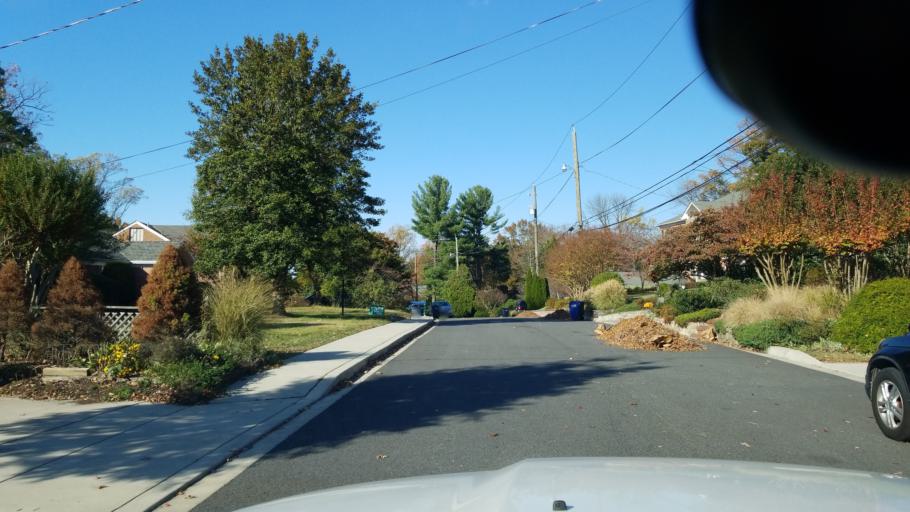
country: US
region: Maryland
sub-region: Montgomery County
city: Chevy Chase
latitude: 38.9829
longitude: -77.0539
